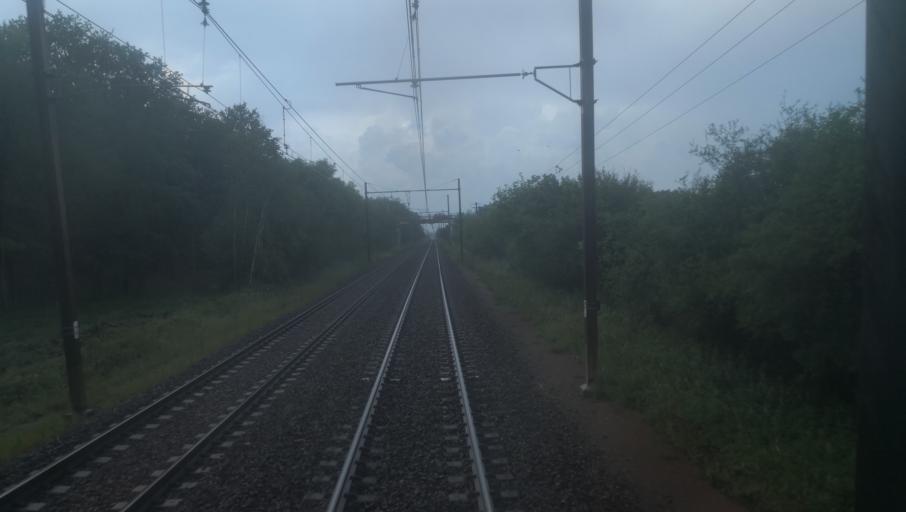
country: FR
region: Centre
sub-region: Departement du Loiret
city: La Ferte-Saint-Aubin
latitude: 47.7015
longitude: 1.9382
